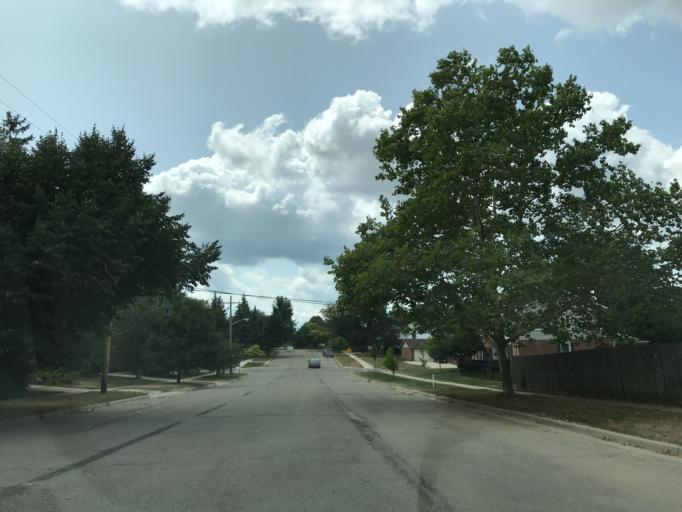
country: US
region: Michigan
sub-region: Washtenaw County
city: Ann Arbor
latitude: 42.2523
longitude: -83.7630
